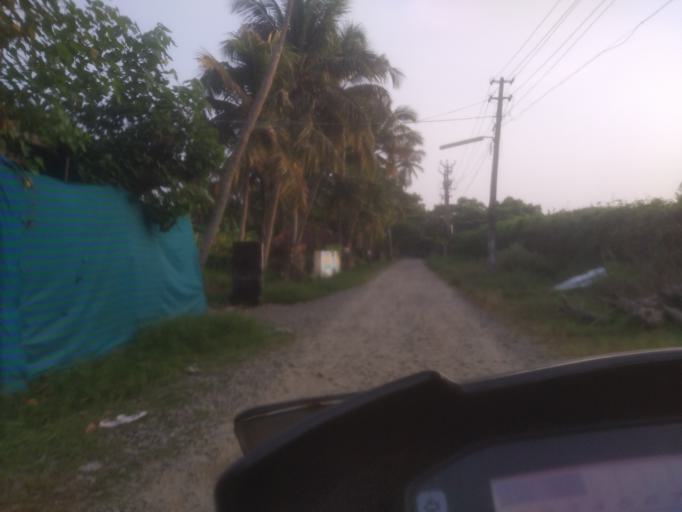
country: IN
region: Kerala
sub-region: Ernakulam
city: Elur
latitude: 10.0187
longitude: 76.2147
